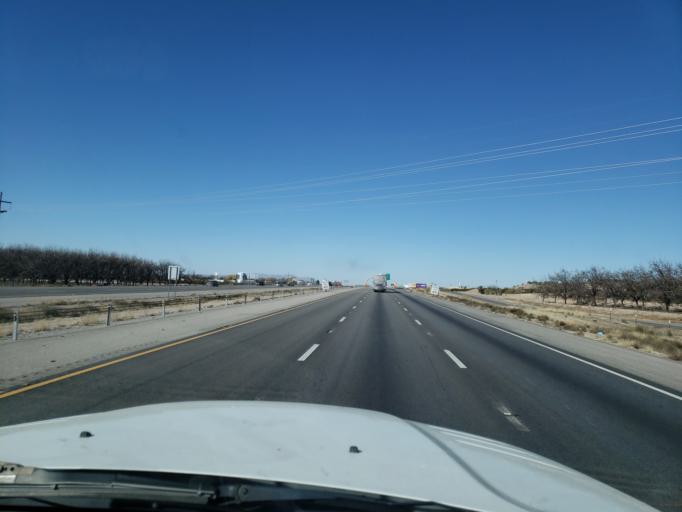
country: US
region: New Mexico
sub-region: Dona Ana County
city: University Park
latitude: 32.2422
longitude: -106.7187
